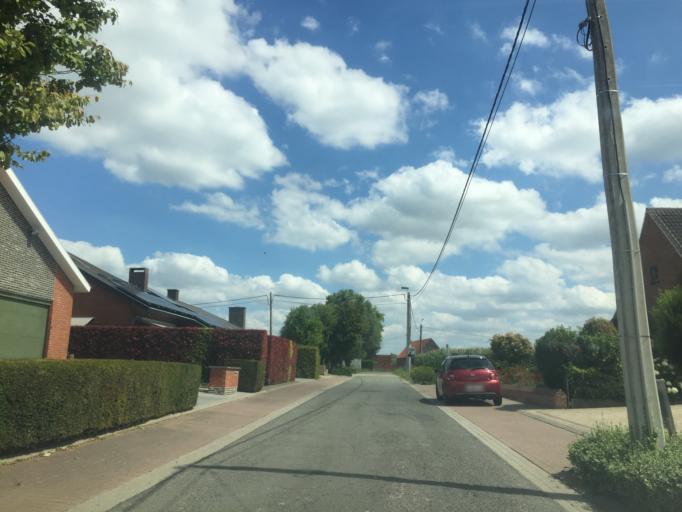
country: BE
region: Flanders
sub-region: Provincie West-Vlaanderen
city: Staden
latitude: 50.9724
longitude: 3.0274
